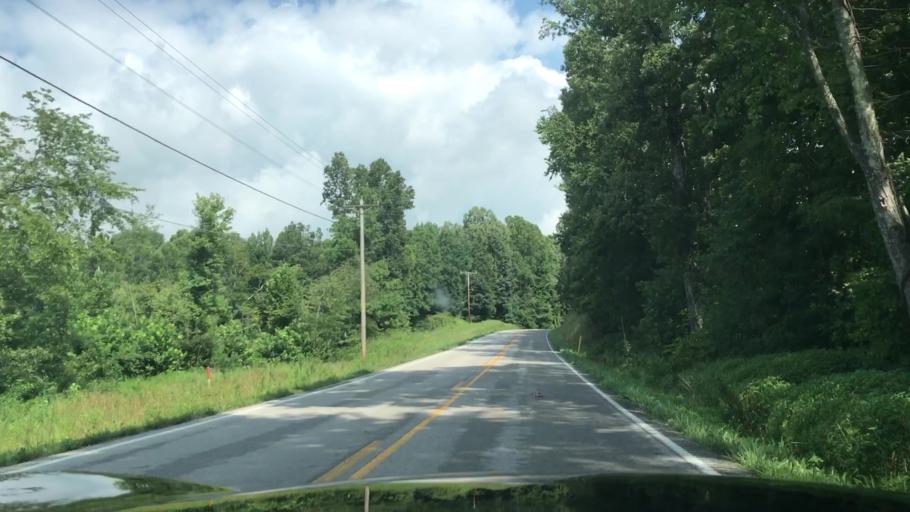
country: US
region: Kentucky
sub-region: Ohio County
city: Oak Grove
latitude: 37.1989
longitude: -86.8861
